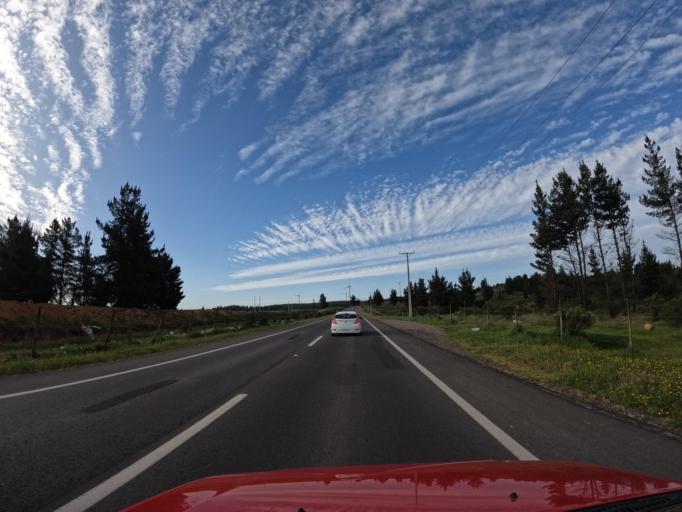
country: CL
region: Valparaiso
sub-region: San Antonio Province
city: San Antonio
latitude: -34.0602
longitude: -71.6259
